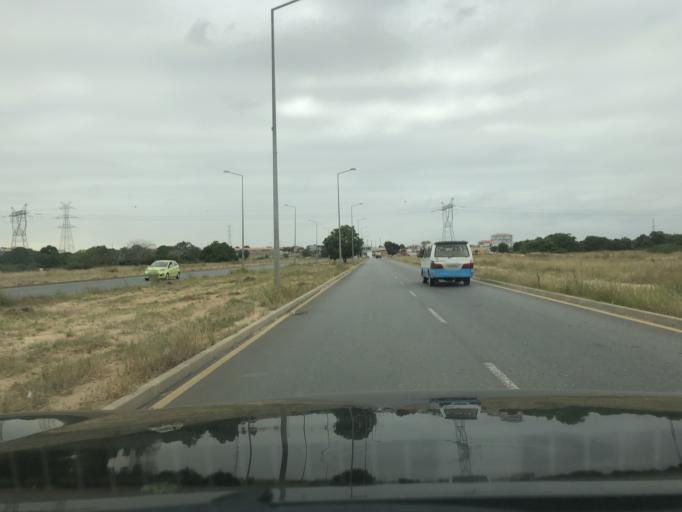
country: AO
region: Luanda
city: Luanda
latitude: -8.9759
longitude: 13.2864
